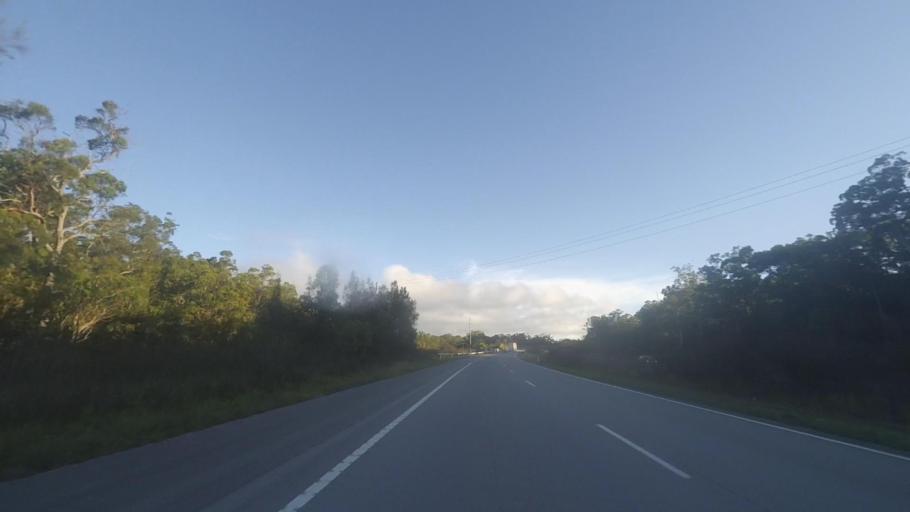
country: AU
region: New South Wales
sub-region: Great Lakes
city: Bulahdelah
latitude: -32.5018
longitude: 152.2103
